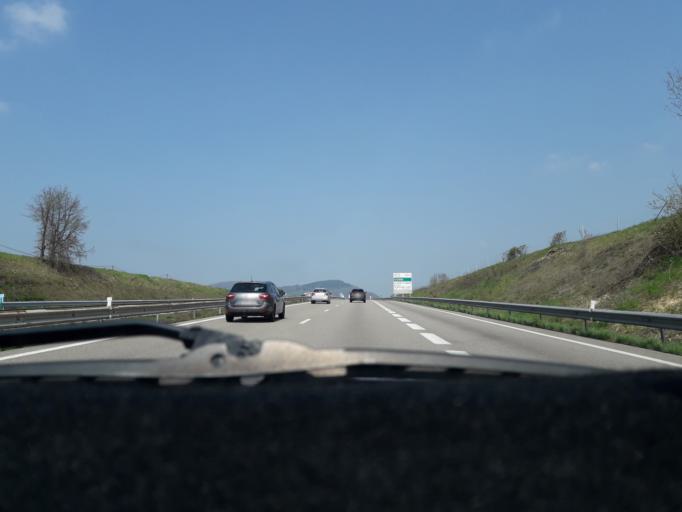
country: FR
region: Rhone-Alpes
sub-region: Departement de l'Isere
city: Apprieu
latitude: 45.3766
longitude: 5.4823
